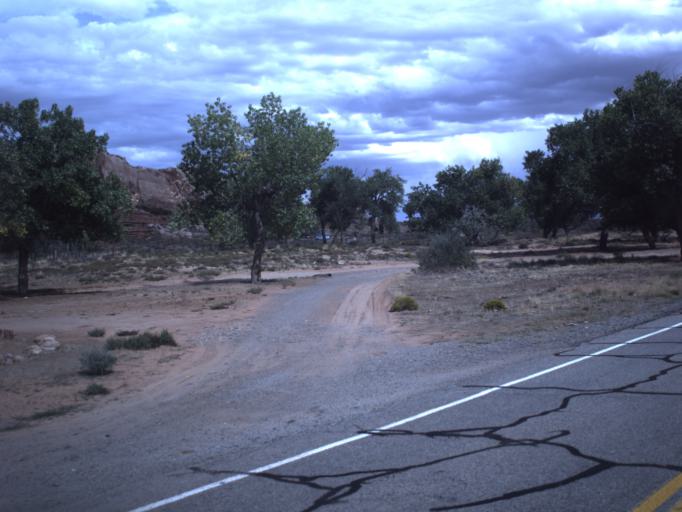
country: US
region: Utah
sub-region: San Juan County
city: Blanding
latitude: 37.2834
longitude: -109.5150
